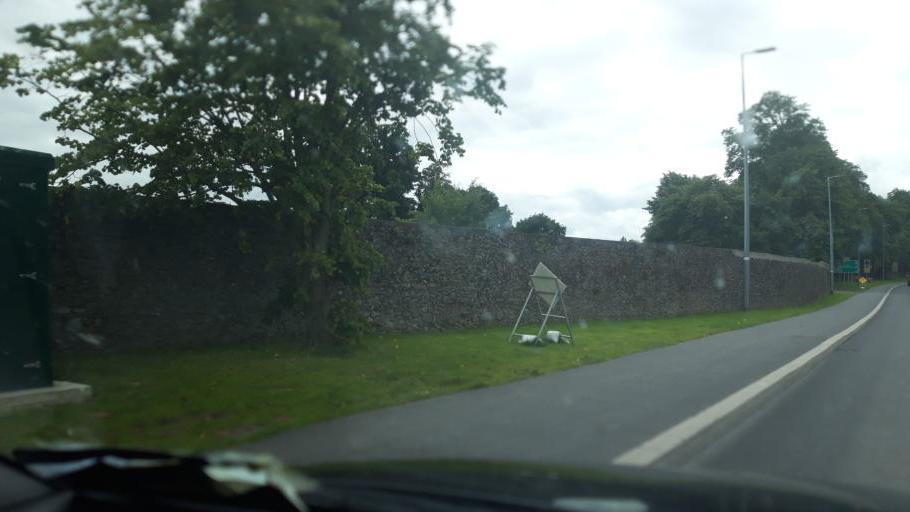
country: IE
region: Leinster
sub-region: Kilkenny
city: Kilkenny
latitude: 52.6404
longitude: -7.2674
